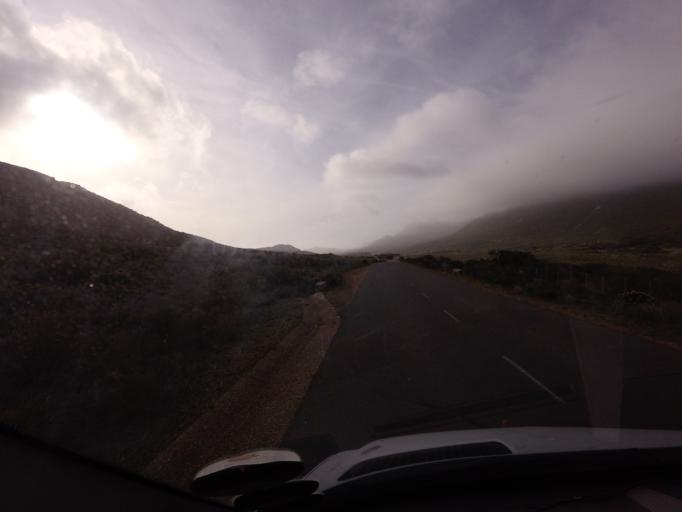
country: ZA
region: Western Cape
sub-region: City of Cape Town
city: Retreat
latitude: -34.2634
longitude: 18.4599
